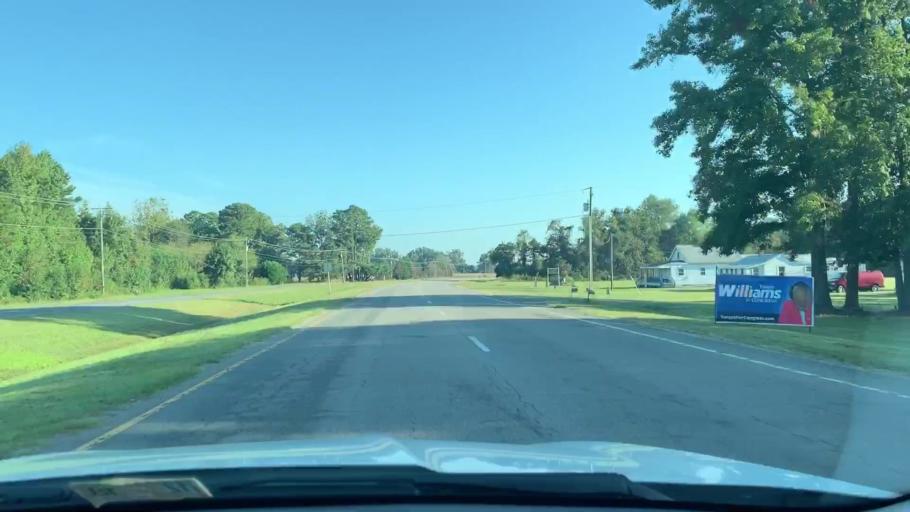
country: US
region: Virginia
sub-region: Lancaster County
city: Kilmarnock
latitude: 37.6668
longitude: -76.3821
